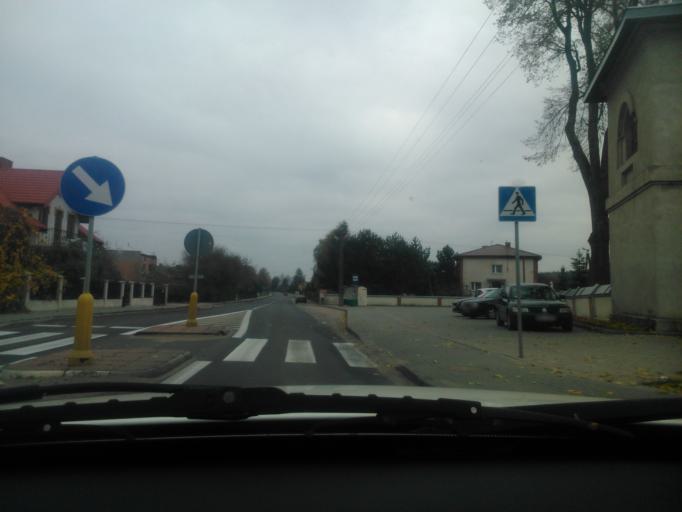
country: PL
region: Masovian Voivodeship
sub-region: Powiat mlawski
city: Lipowiec Koscielny
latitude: 53.1041
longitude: 20.1765
